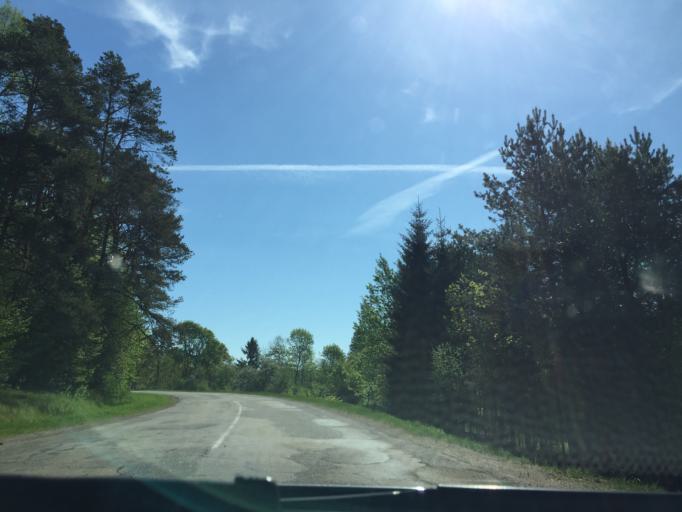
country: LV
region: Ropazu
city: Ropazi
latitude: 57.0068
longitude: 24.5739
